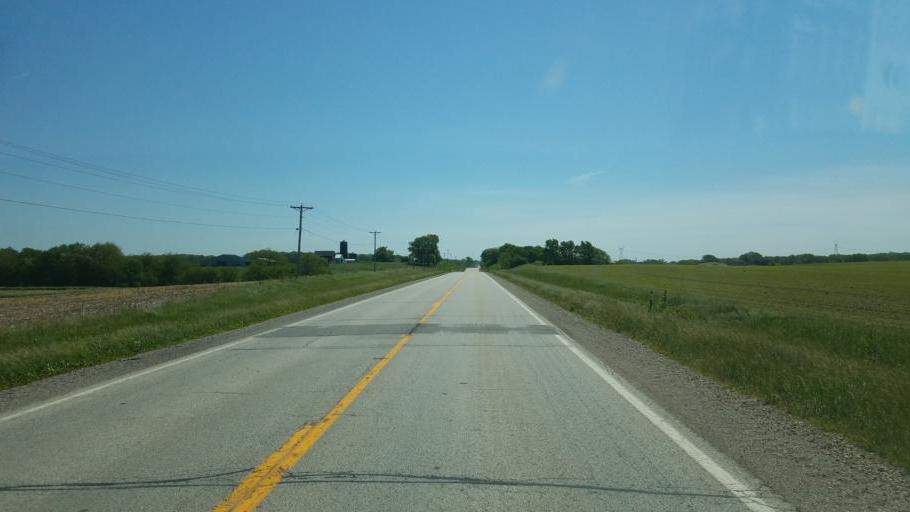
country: US
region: Illinois
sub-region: McLean County
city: Heyworth
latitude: 40.3121
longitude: -89.0331
